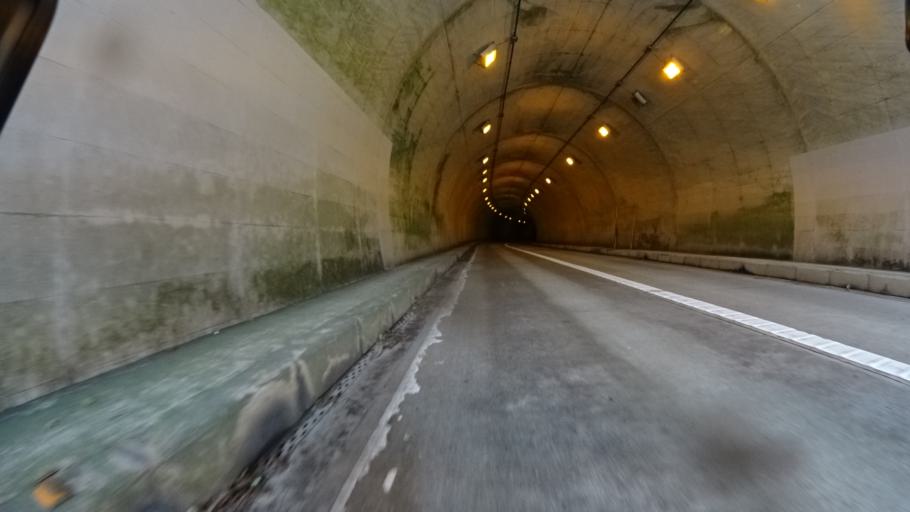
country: JP
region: Tokyo
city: Ome
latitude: 35.8388
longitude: 139.1992
